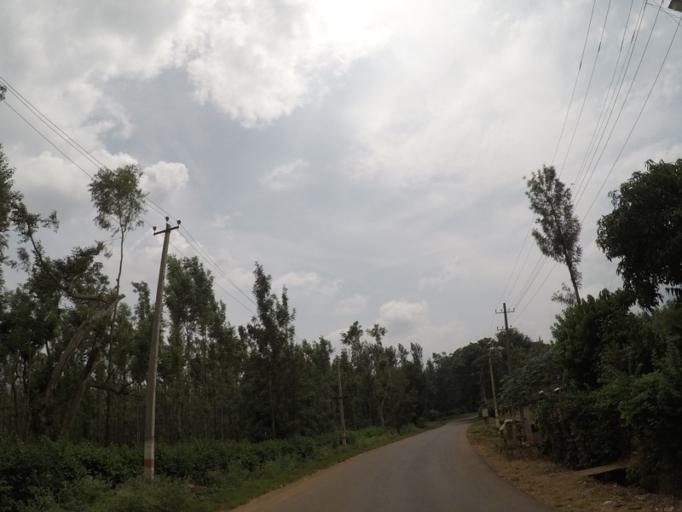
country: IN
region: Karnataka
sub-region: Chikmagalur
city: Chikmagalur
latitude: 13.4327
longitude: 75.8091
